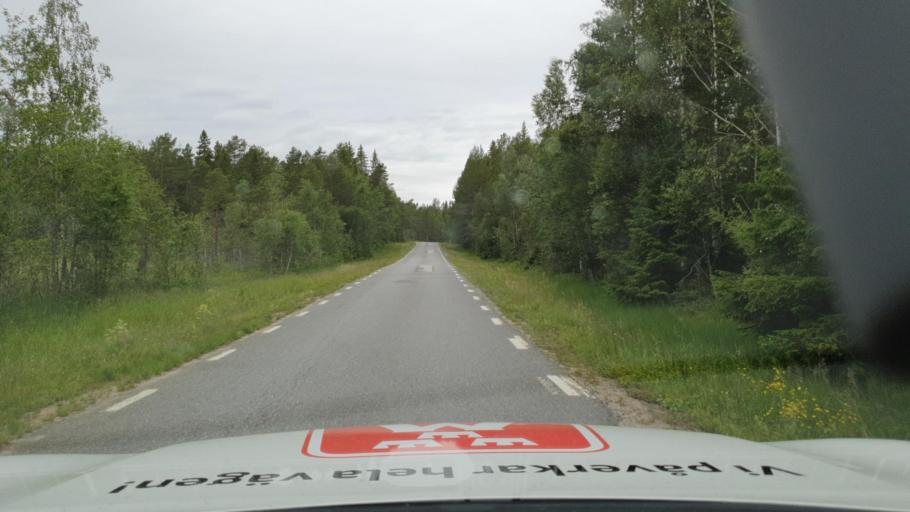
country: SE
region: Vaesterbotten
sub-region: Nordmalings Kommun
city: Nordmaling
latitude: 63.4331
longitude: 19.4810
